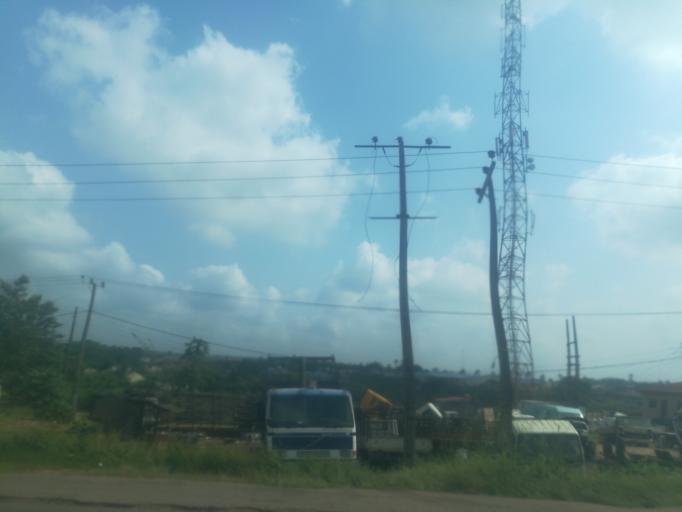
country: NG
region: Oyo
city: Ibadan
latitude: 7.4423
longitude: 3.9229
